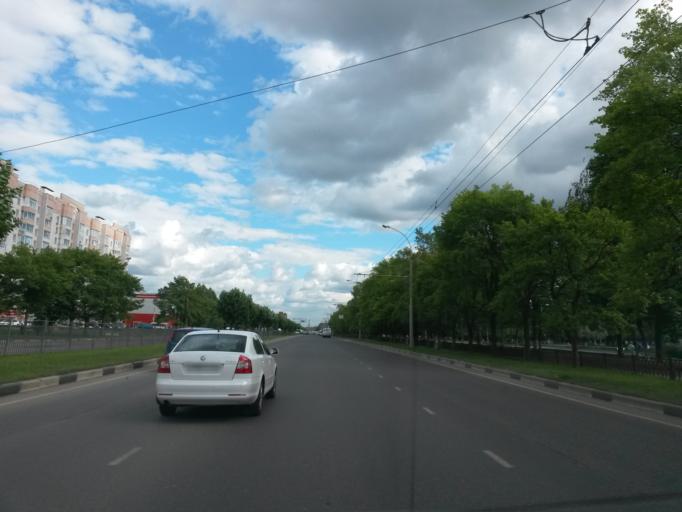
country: RU
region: Jaroslavl
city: Yaroslavl
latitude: 57.6881
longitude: 39.7806
